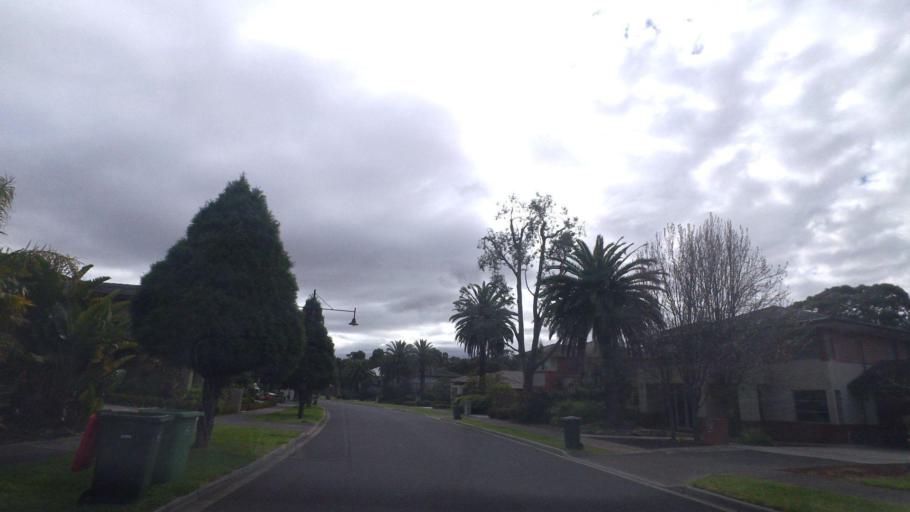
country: AU
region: Victoria
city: Macleod
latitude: -37.7195
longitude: 145.0599
